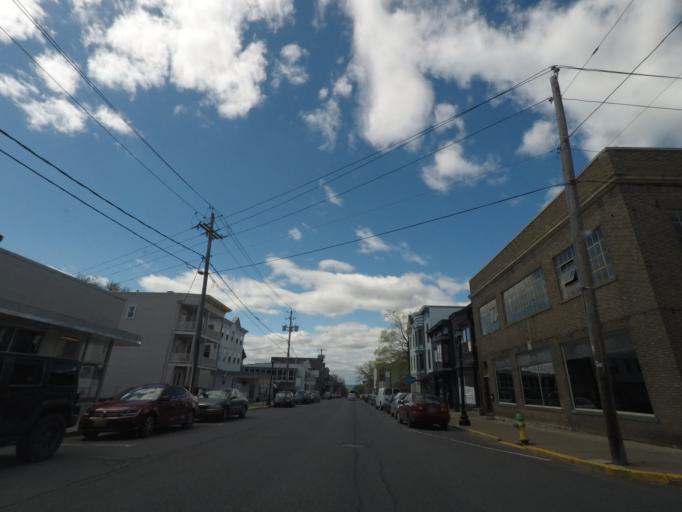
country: US
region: New York
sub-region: Columbia County
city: Oakdale
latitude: 42.2460
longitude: -73.7817
